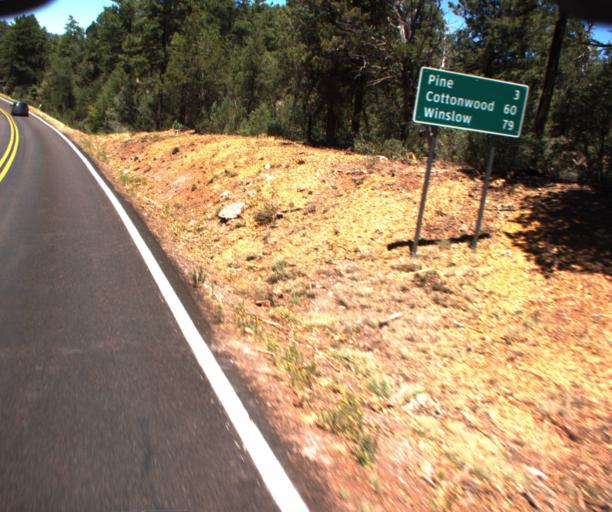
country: US
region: Arizona
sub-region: Gila County
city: Pine
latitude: 34.3627
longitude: -111.4269
